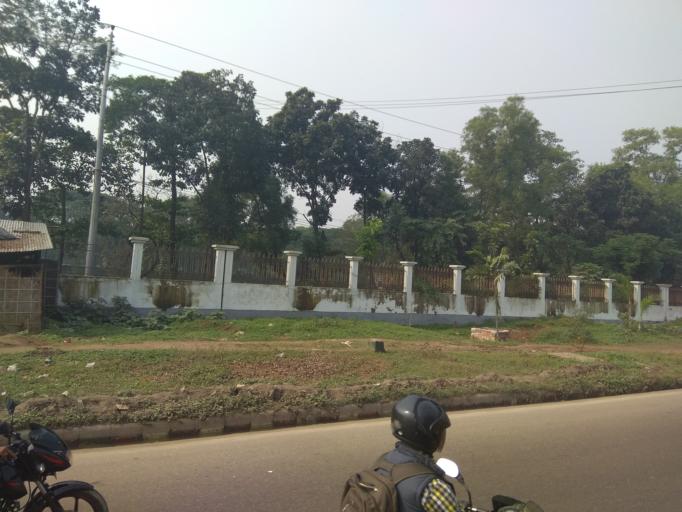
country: BD
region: Dhaka
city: Tungi
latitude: 23.8391
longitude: 90.4176
